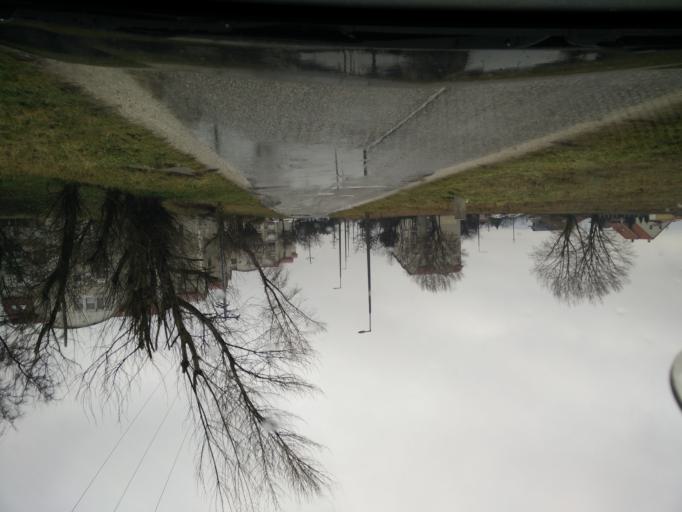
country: HU
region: Pest
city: Pilisszentivan
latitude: 47.6108
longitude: 18.9017
